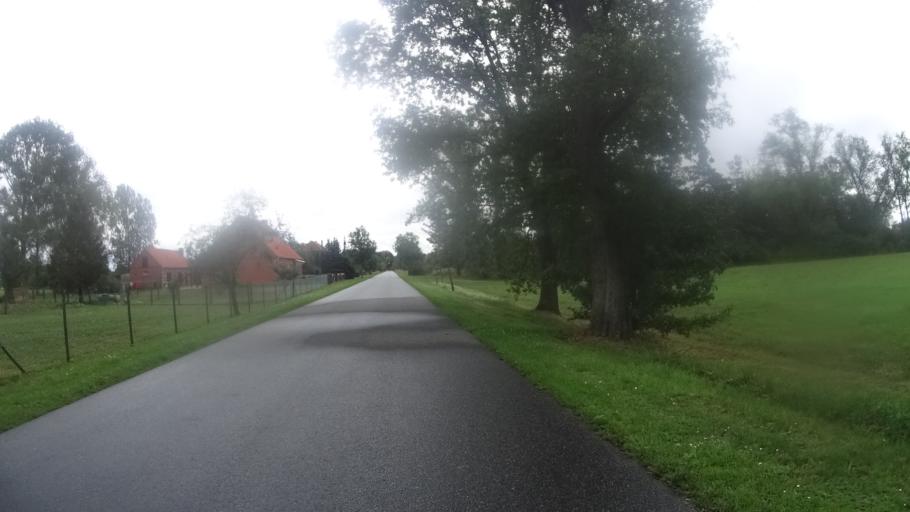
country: DE
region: Lower Saxony
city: Neu Darchau
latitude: 53.2433
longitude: 10.8893
